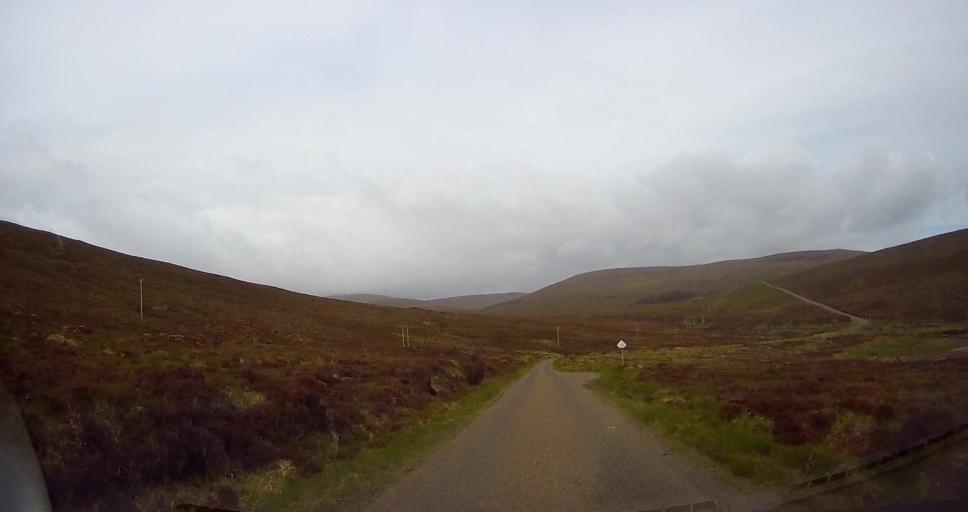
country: GB
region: Scotland
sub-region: Orkney Islands
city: Stromness
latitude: 58.8684
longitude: -3.2281
